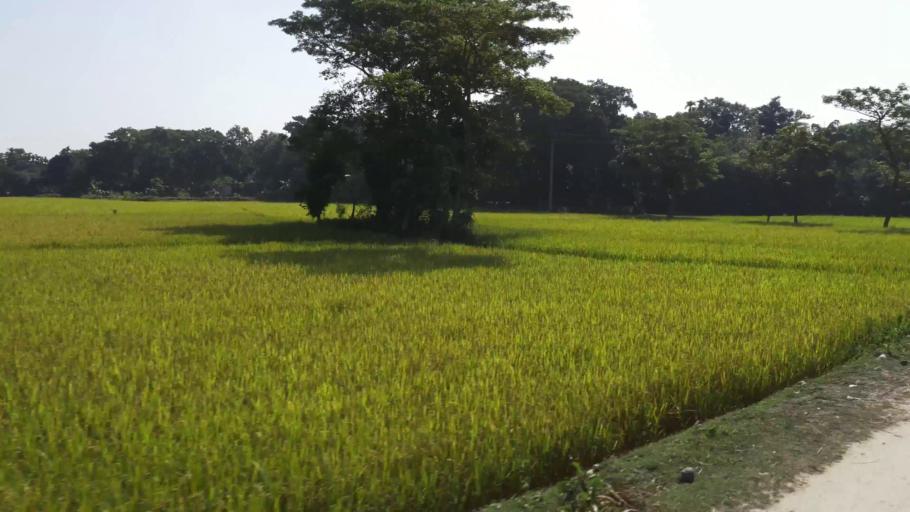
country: BD
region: Dhaka
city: Gafargaon
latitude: 24.4906
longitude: 90.5264
